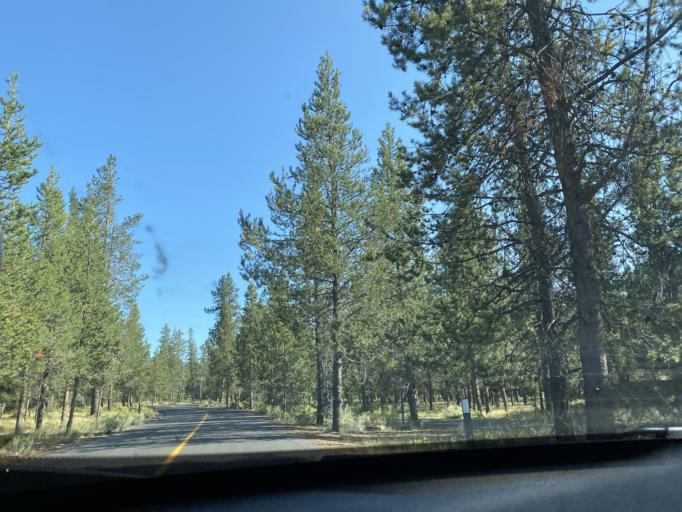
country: US
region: Oregon
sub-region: Deschutes County
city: Sunriver
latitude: 43.8954
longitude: -121.4393
